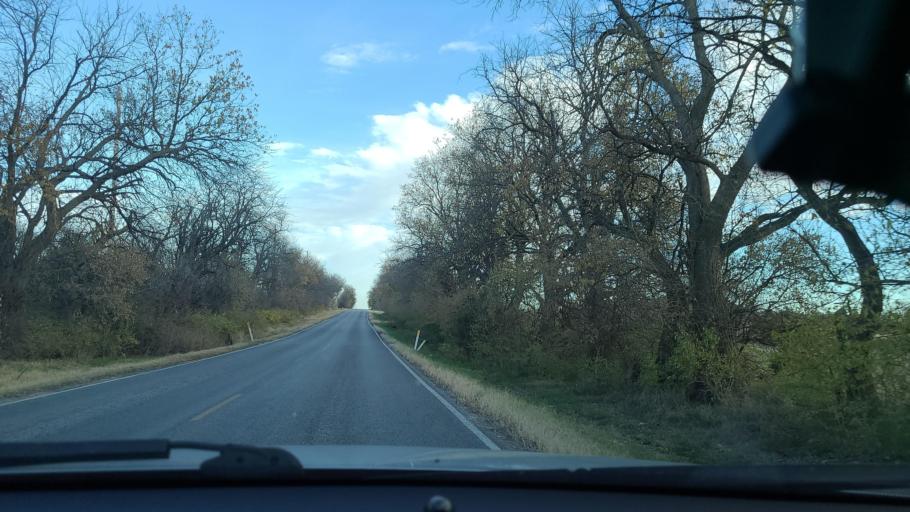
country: US
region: Kansas
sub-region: Sedgwick County
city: Goddard
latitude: 37.6497
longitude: -97.5496
